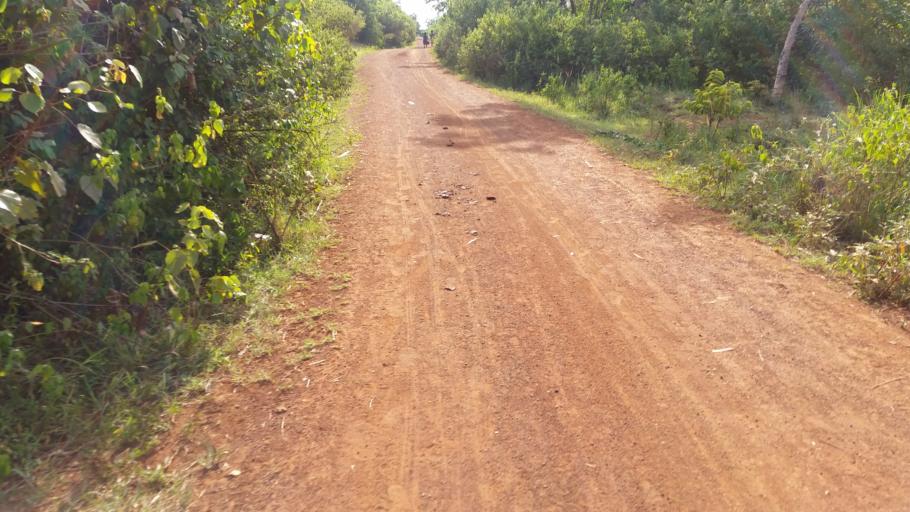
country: UG
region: Eastern Region
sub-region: Busia District
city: Busia
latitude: 0.5497
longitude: 34.0032
